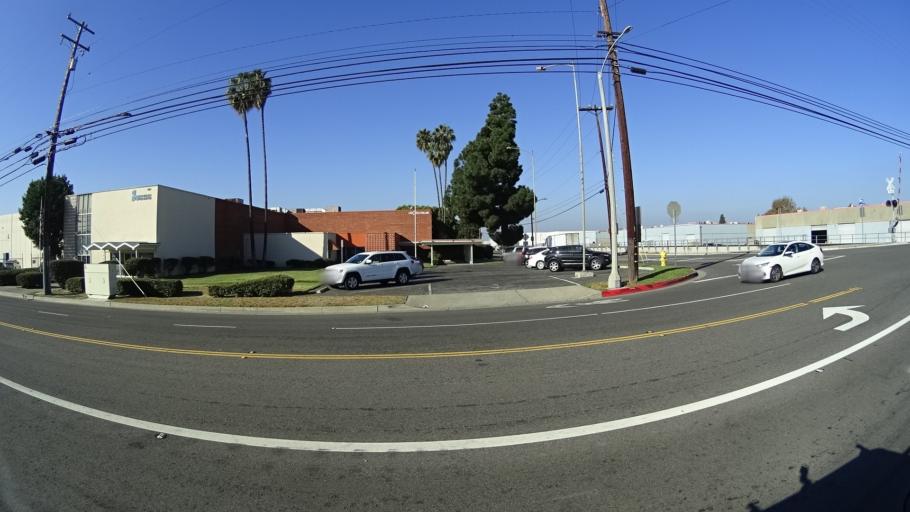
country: US
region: California
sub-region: Orange County
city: Fullerton
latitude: 33.8666
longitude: -117.8982
